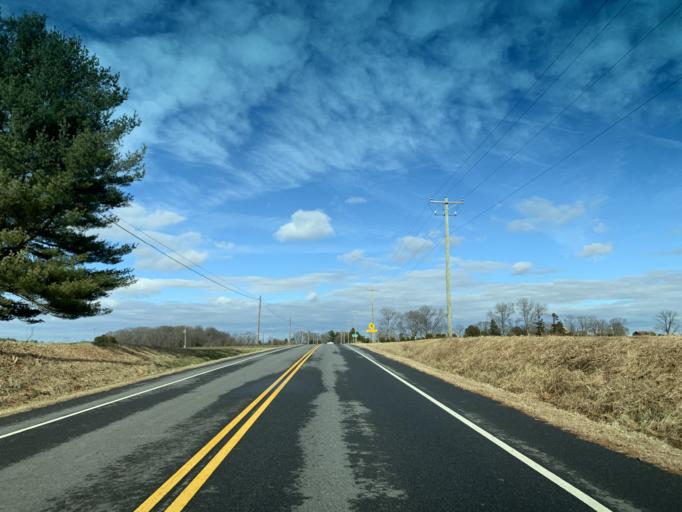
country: US
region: Maryland
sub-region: Kent County
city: Chestertown
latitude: 39.3413
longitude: -76.0621
